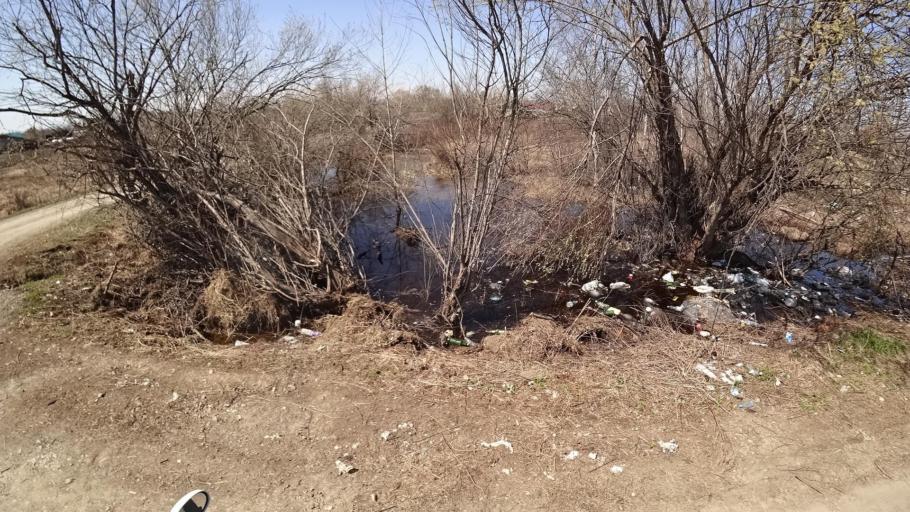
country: RU
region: Khabarovsk Krai
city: Khurba
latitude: 50.4040
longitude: 136.8837
